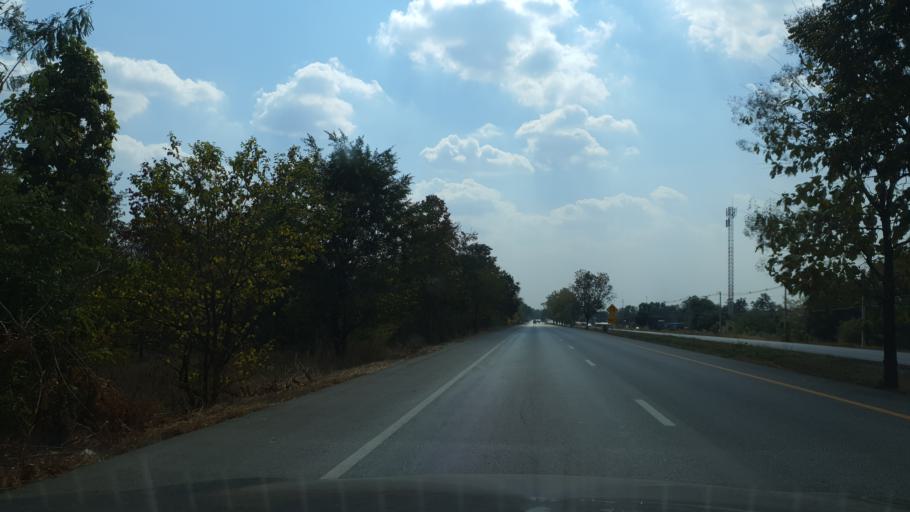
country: TH
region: Tak
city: Sam Ngao
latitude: 17.2924
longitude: 99.1425
